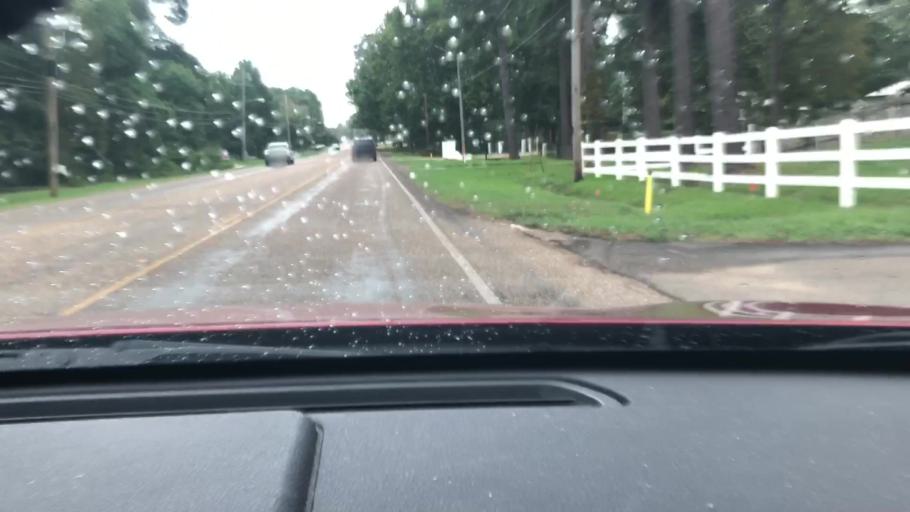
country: US
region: Texas
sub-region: Bowie County
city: Nash
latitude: 33.4426
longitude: -94.1176
